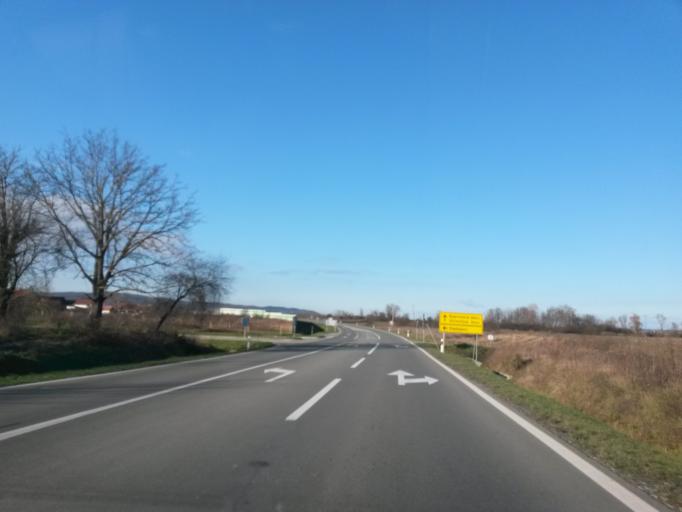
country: HR
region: Virovitick-Podravska
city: Slatina
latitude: 45.7295
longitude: 17.6604
